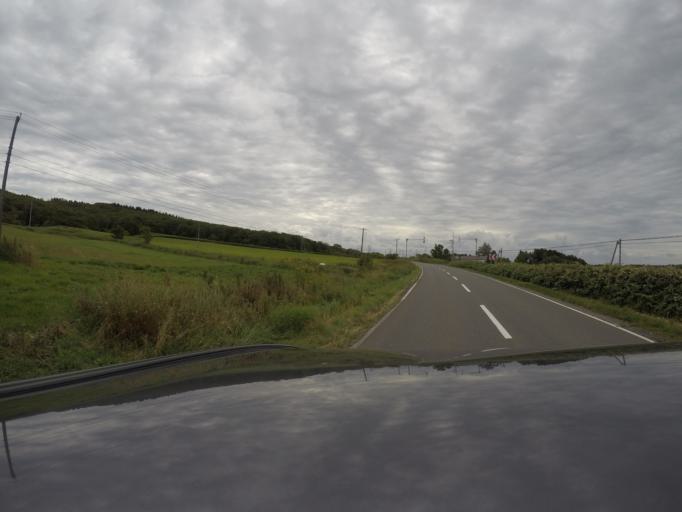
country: JP
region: Hokkaido
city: Makubetsu
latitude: 45.2080
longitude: 141.7345
